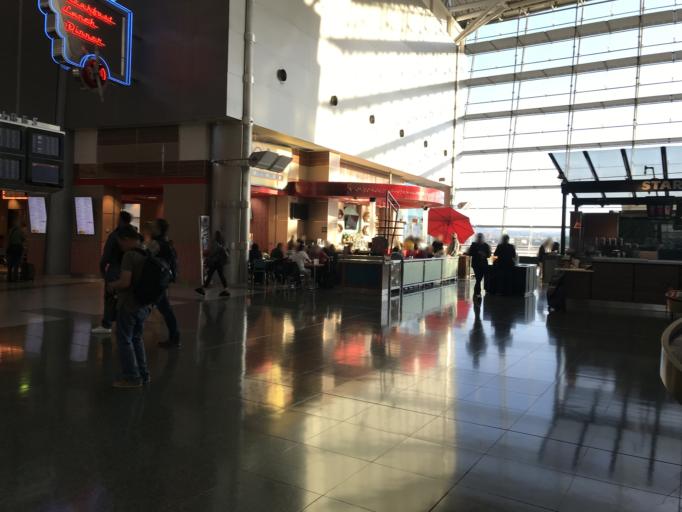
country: US
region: Nevada
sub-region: Clark County
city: Paradise
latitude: 36.0819
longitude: -115.1380
